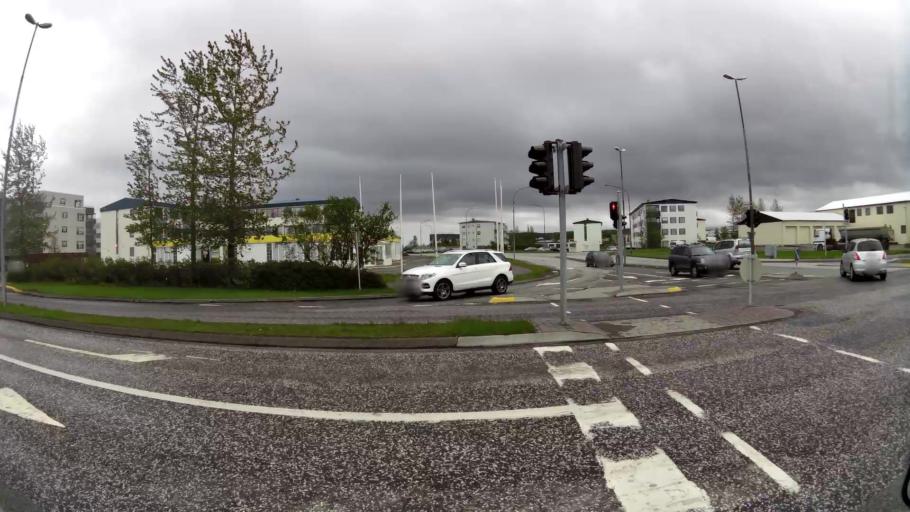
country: IS
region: Capital Region
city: Hafnarfjoerdur
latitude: 64.0755
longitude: -21.9520
